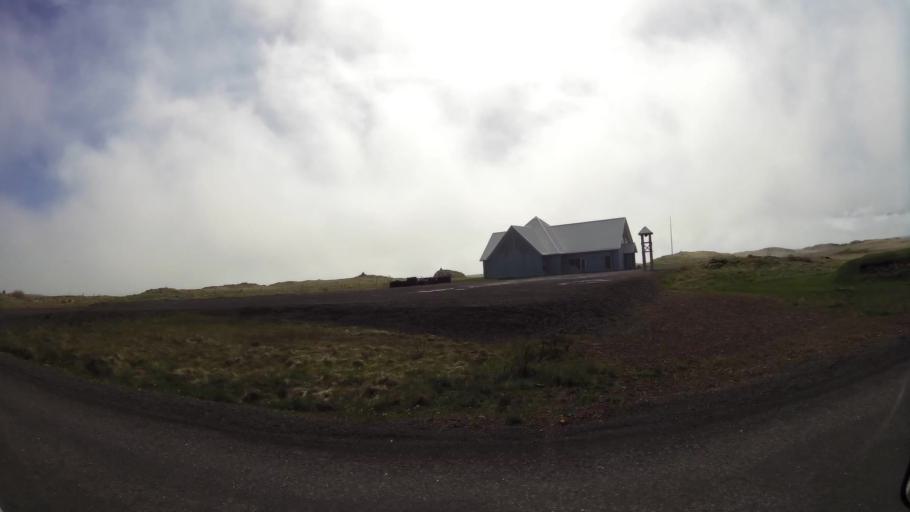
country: IS
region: East
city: Reydarfjoerdur
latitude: 64.6541
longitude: -14.2985
